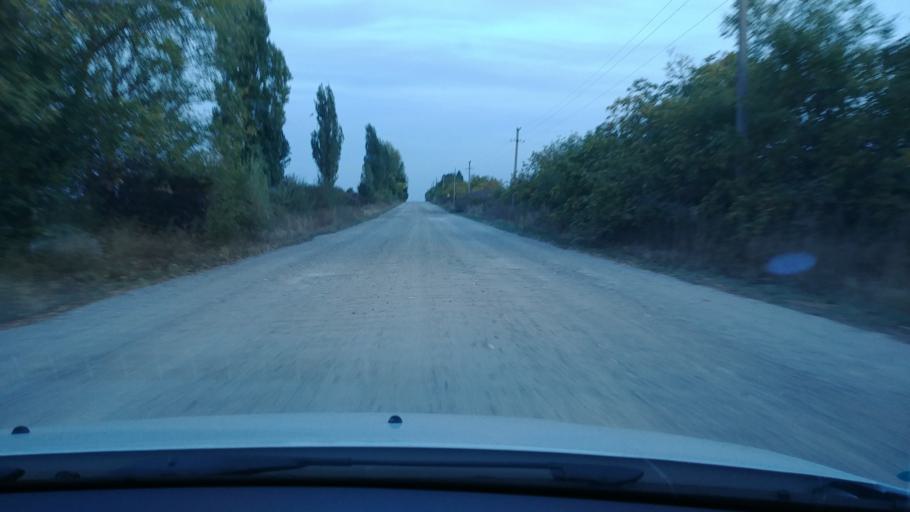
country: MD
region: Rezina
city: Saharna
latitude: 47.6715
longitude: 28.9400
